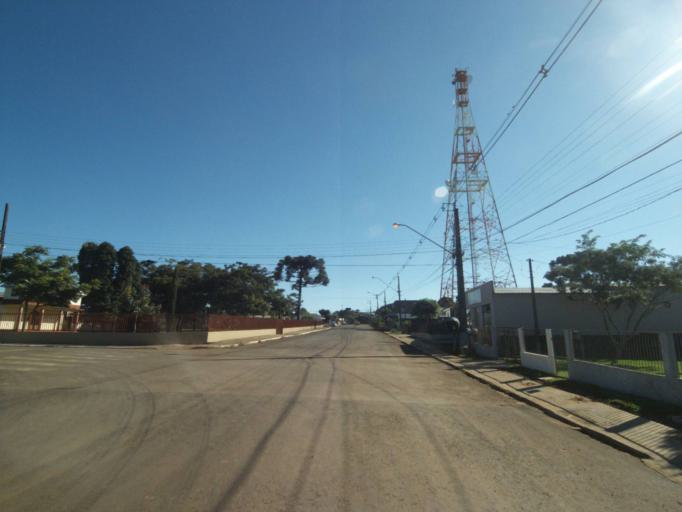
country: BR
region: Parana
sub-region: Pinhao
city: Pinhao
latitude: -25.8399
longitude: -52.0280
